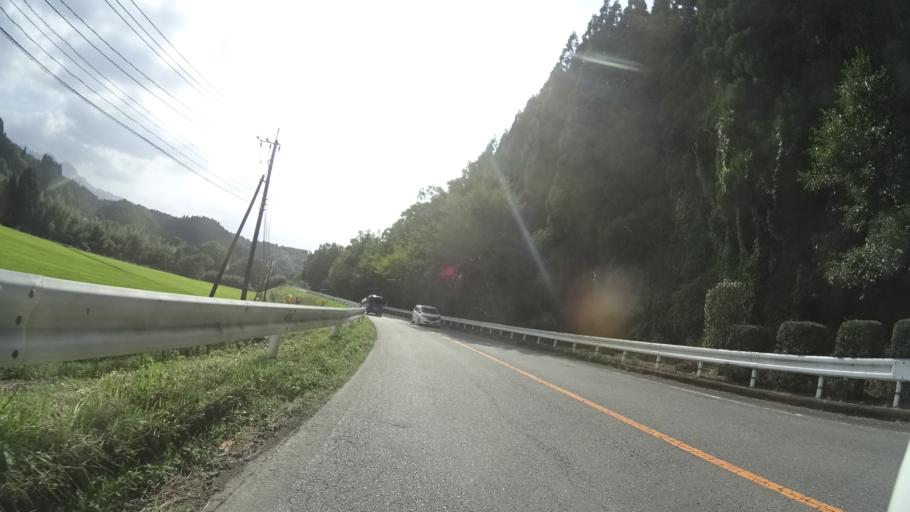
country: JP
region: Kumamoto
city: Aso
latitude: 32.6879
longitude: 131.0808
